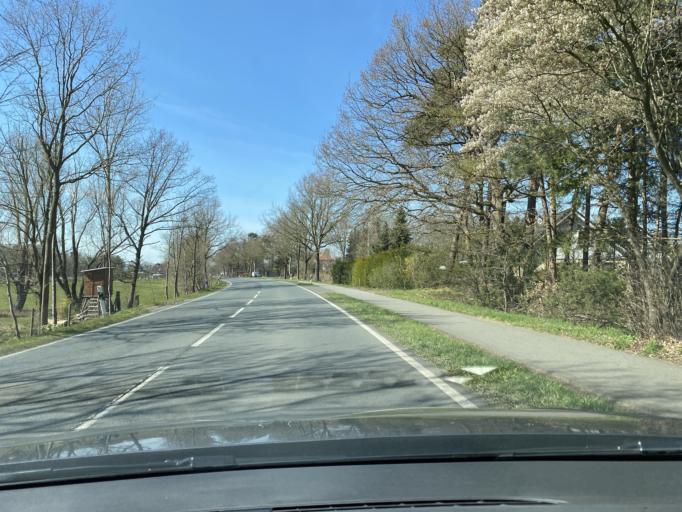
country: DE
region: Lower Saxony
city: Grasberg
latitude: 53.1314
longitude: 8.9964
